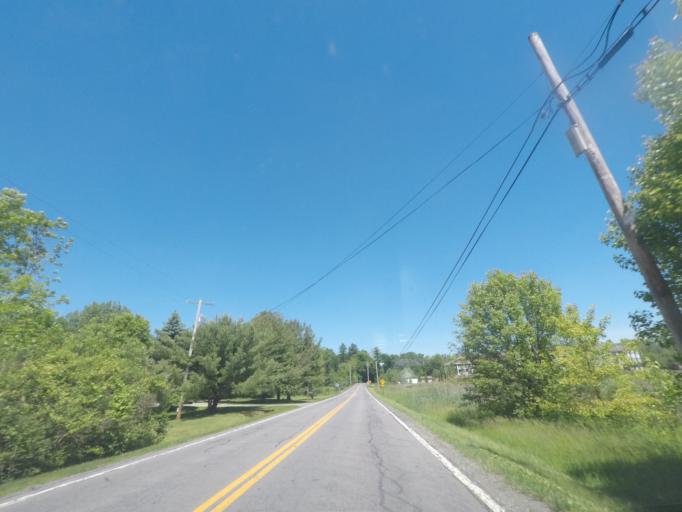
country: US
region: New York
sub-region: Saratoga County
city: Country Knolls
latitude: 42.8657
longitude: -73.8477
